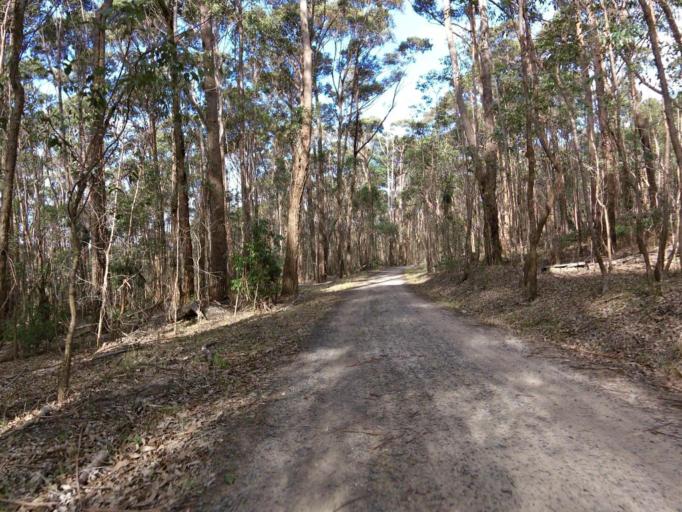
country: AU
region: Victoria
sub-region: Yarra Ranges
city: Lysterfield
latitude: -37.9417
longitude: 145.2792
